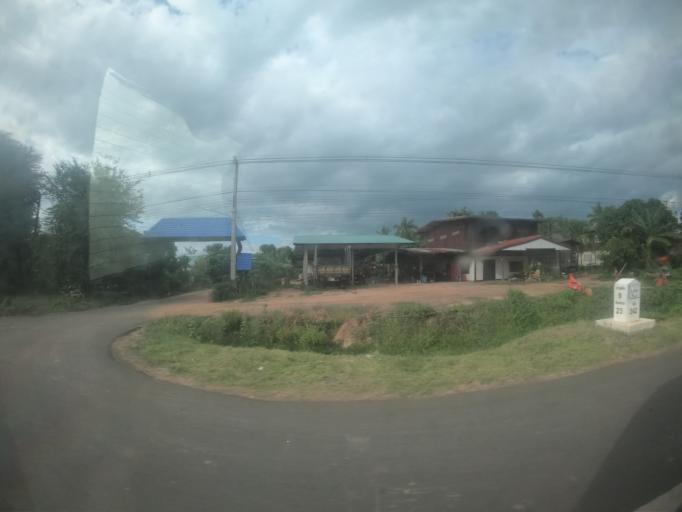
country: TH
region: Surin
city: Kap Choeng
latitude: 14.5305
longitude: 103.5312
